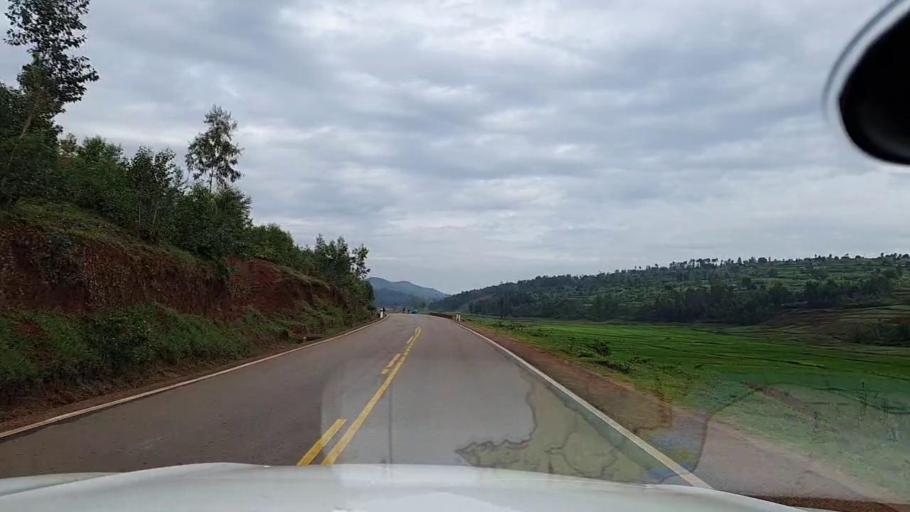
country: RW
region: Southern Province
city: Butare
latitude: -2.5695
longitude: 29.7300
